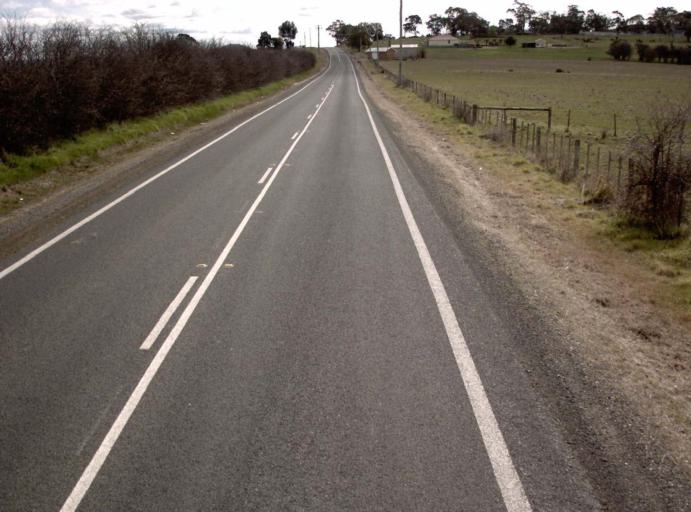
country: AU
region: Tasmania
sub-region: Northern Midlands
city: Evandale
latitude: -41.5017
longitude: 147.2495
